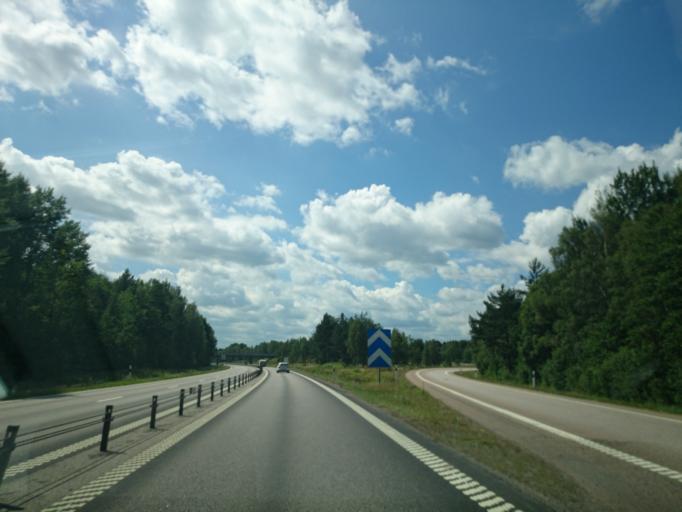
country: SE
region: Kalmar
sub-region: Kalmar Kommun
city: Lindsdal
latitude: 56.7607
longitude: 16.3123
